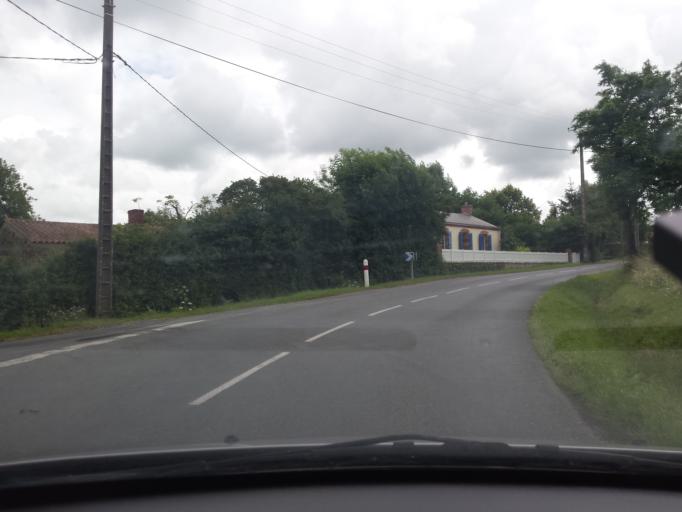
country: FR
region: Pays de la Loire
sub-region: Departement de la Vendee
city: Beaulieu-sous-la-Roche
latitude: 46.6755
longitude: -1.6011
